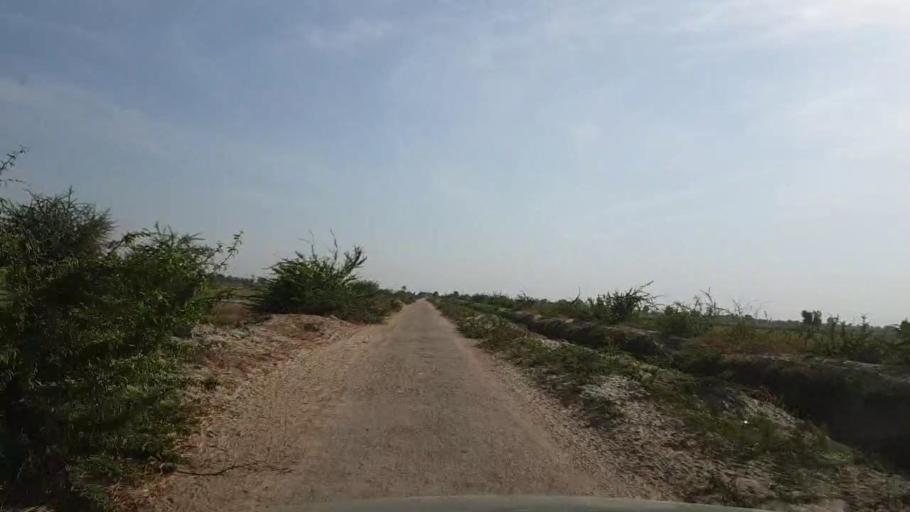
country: PK
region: Sindh
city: Kunri
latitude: 25.1339
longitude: 69.4576
